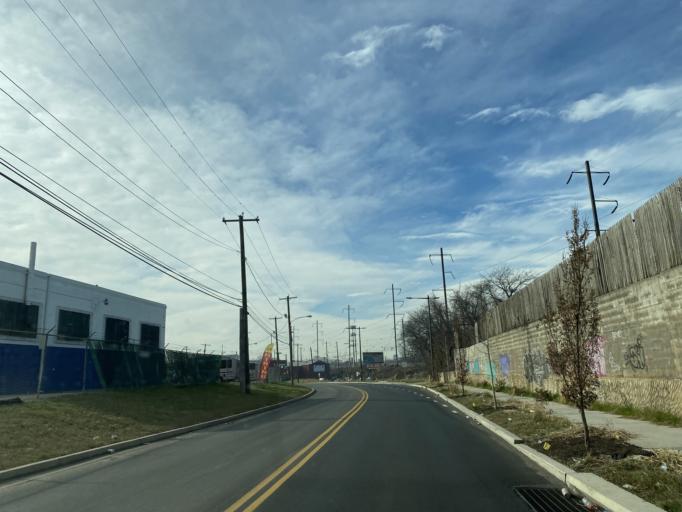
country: US
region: New Jersey
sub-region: Burlington County
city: Palmyra
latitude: 40.0066
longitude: -75.0846
